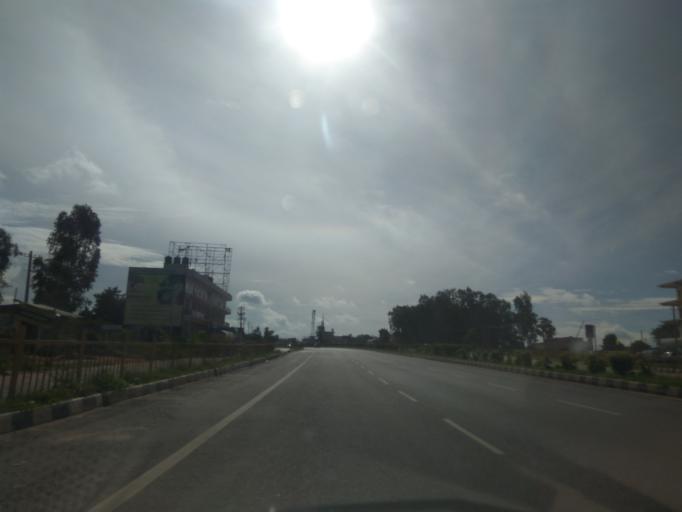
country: IN
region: Karnataka
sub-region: Bangalore Rural
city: Hoskote
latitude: 13.0771
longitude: 77.8045
